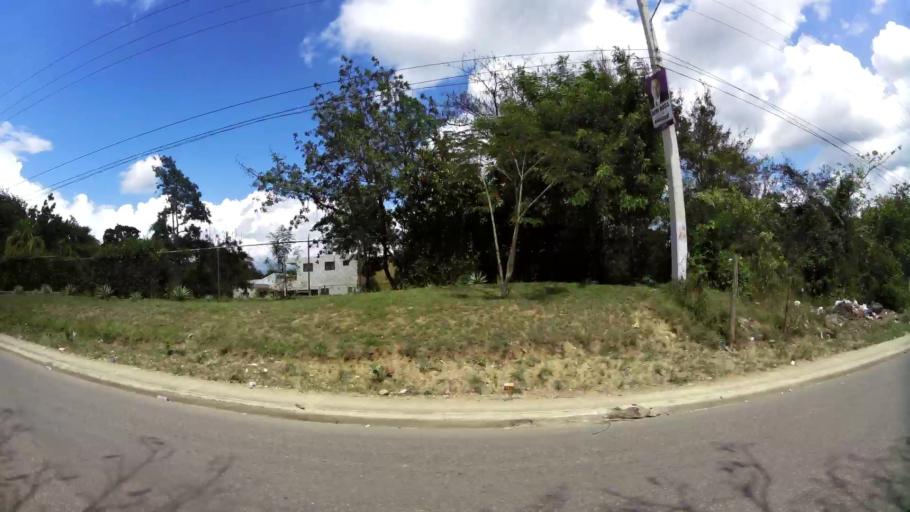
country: DO
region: Santiago
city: Santiago de los Caballeros
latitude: 19.4139
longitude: -70.6766
